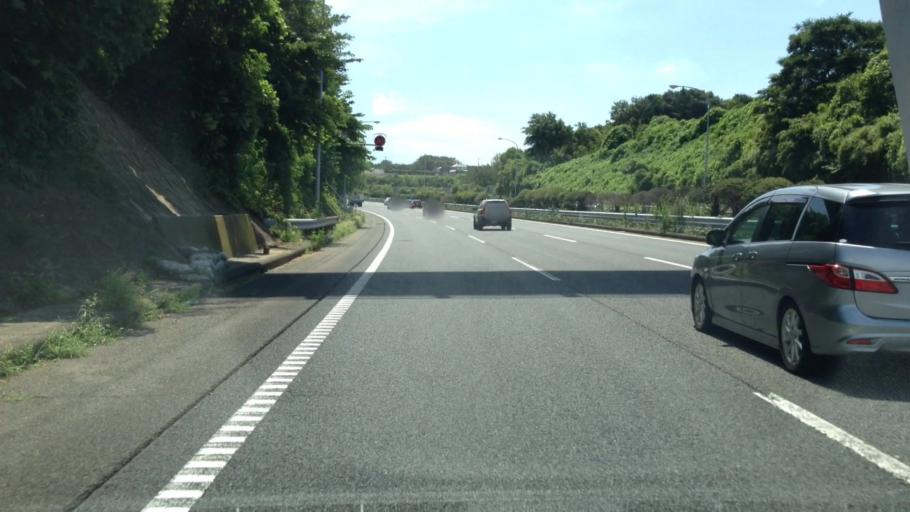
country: JP
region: Kanagawa
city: Yokohama
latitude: 35.4992
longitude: 139.5915
